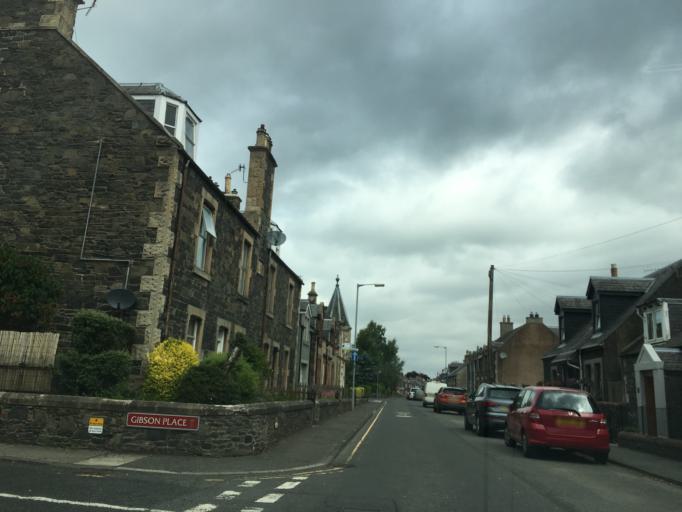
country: GB
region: Scotland
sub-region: The Scottish Borders
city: Peebles
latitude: 55.6525
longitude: -3.1956
